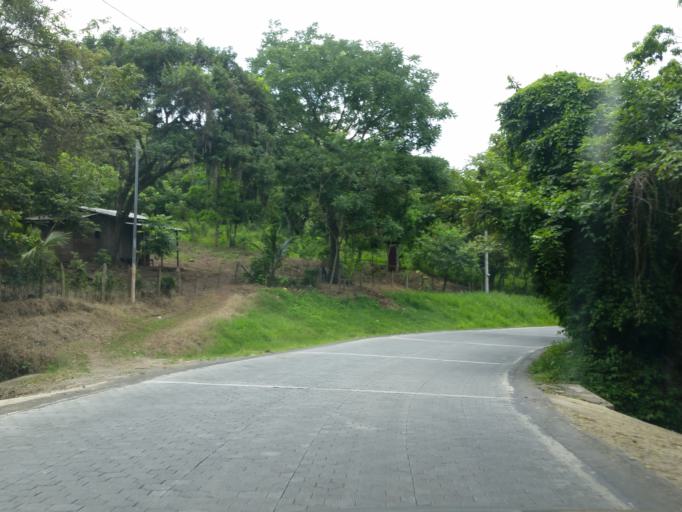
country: NI
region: Matagalpa
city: San Ramon
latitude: 12.9336
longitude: -85.8551
